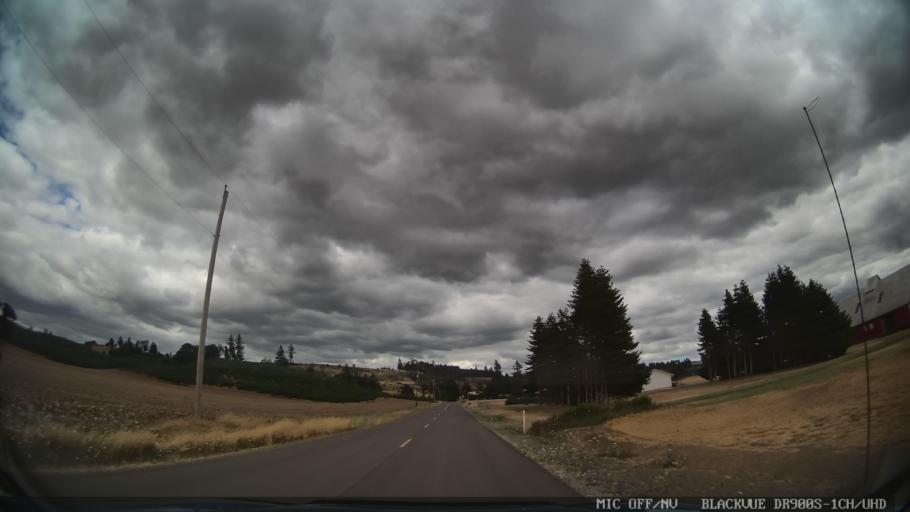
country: US
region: Oregon
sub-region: Marion County
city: Sublimity
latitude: 44.8726
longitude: -122.7131
